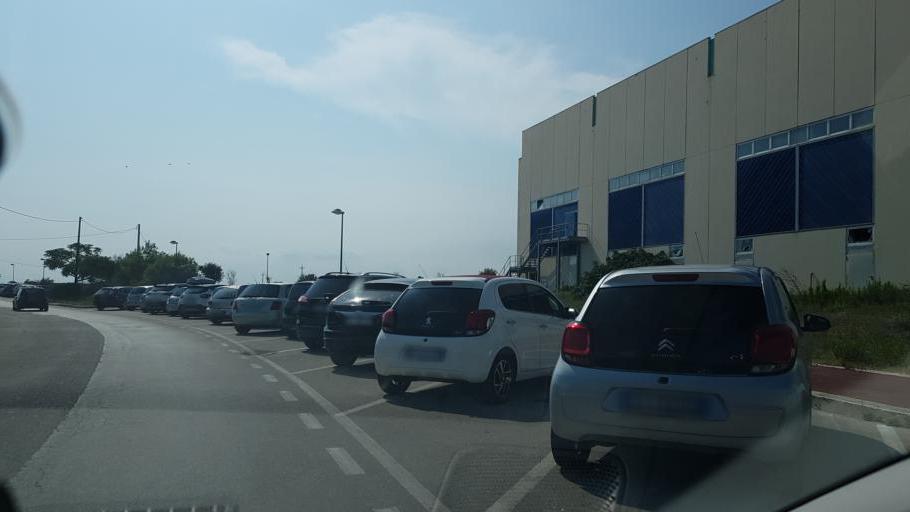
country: IT
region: Apulia
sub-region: Provincia di Bari
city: Monopoli
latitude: 40.9387
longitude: 17.3165
